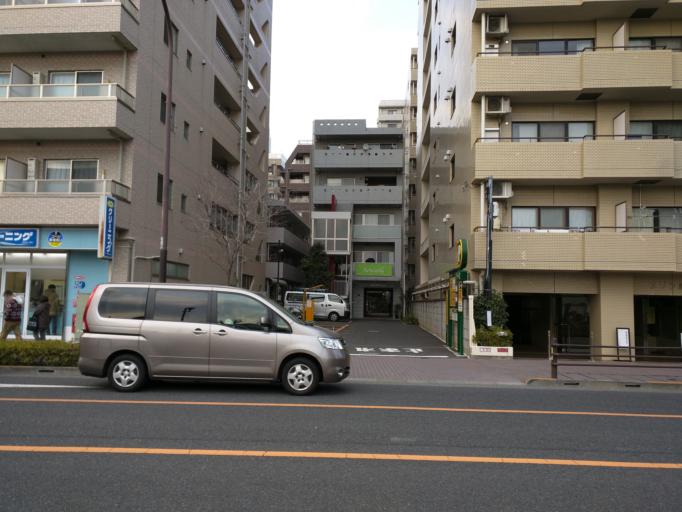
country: JP
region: Tokyo
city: Kokubunji
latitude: 35.6700
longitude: 139.4832
